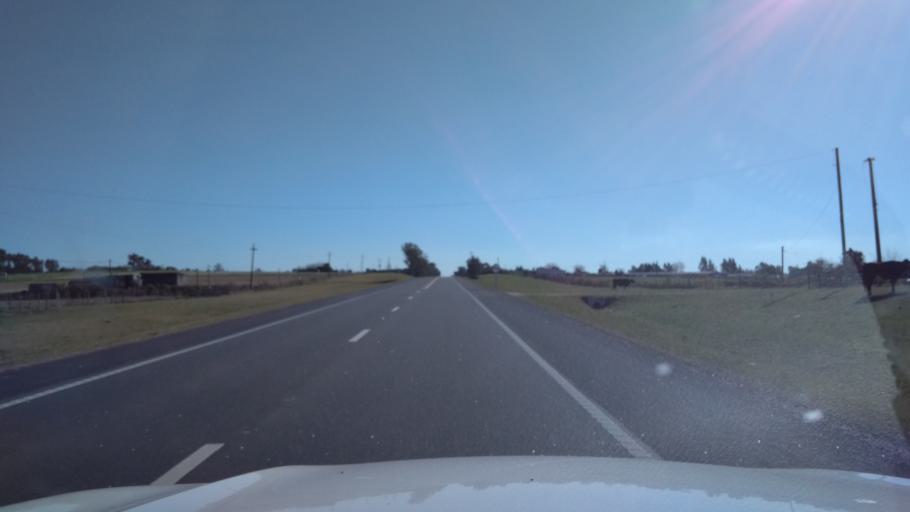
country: UY
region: Canelones
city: Santa Rosa
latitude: -34.5259
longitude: -55.9646
